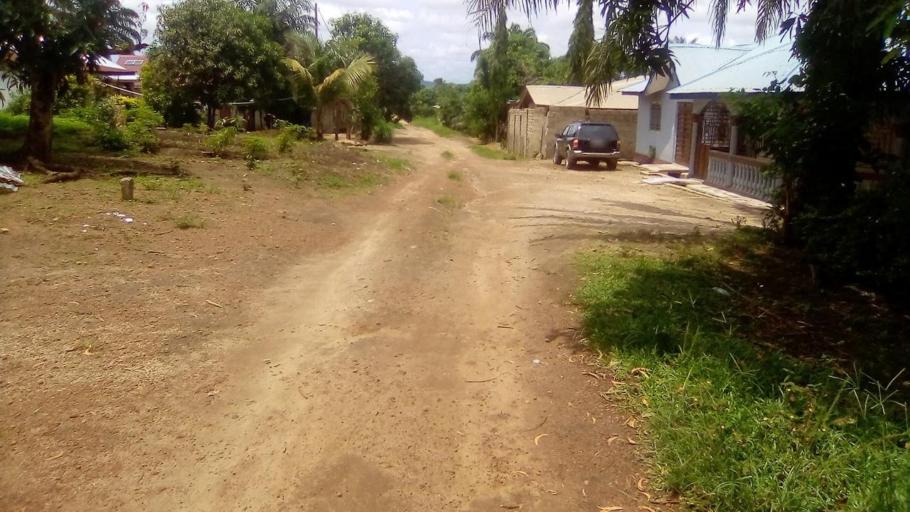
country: SL
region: Southern Province
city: Bo
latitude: 7.9389
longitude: -11.7432
